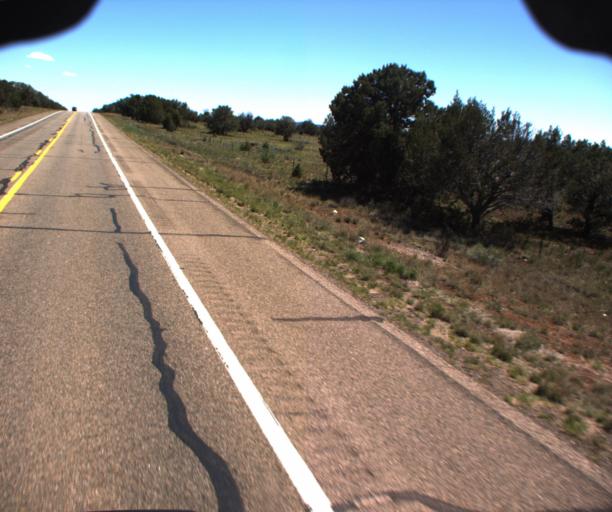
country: US
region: Arizona
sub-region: Coconino County
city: Williams
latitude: 35.1705
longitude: -112.4608
